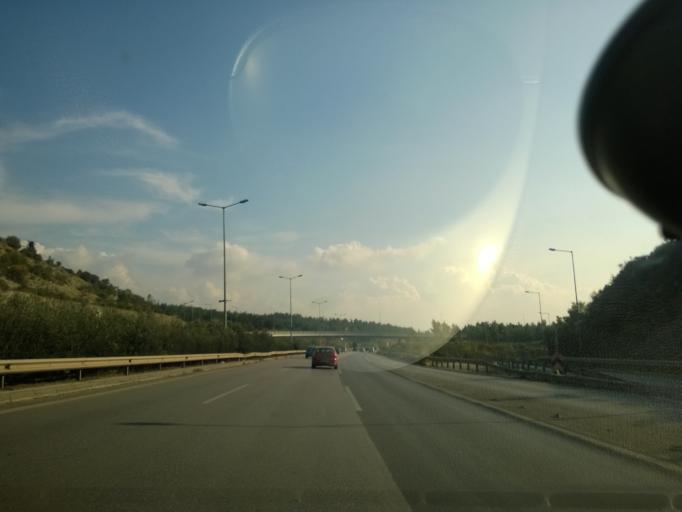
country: GR
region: Central Macedonia
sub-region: Nomos Thessalonikis
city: Triandria
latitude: 40.6242
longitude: 22.9808
